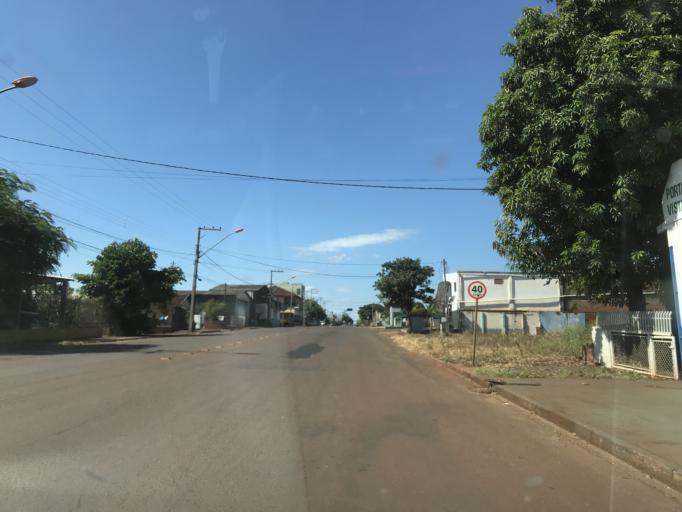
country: BR
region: Parana
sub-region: Palotina
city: Palotina
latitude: -24.2858
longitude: -53.8492
